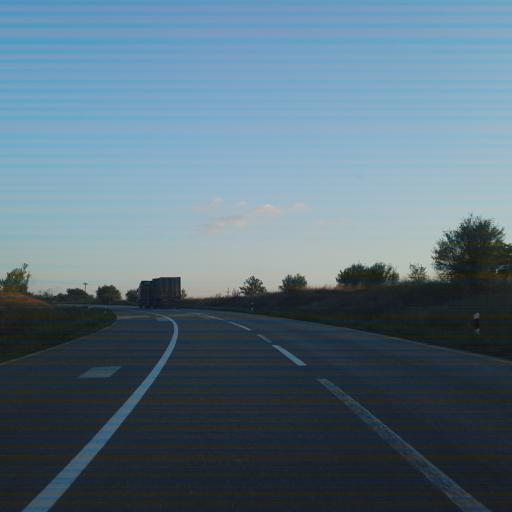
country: RS
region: Central Serbia
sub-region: Zajecarski Okrug
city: Zajecar
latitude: 44.0326
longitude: 22.3418
